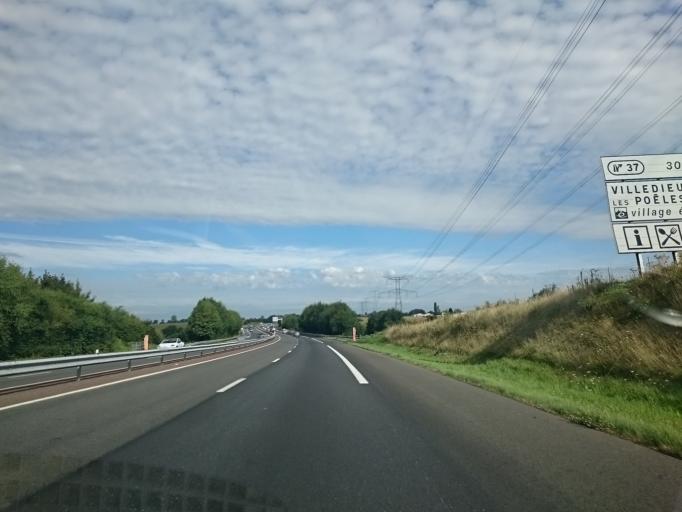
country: FR
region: Lower Normandy
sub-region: Departement de la Manche
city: Villedieu-les-Poeles
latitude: 48.8339
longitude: -1.2455
